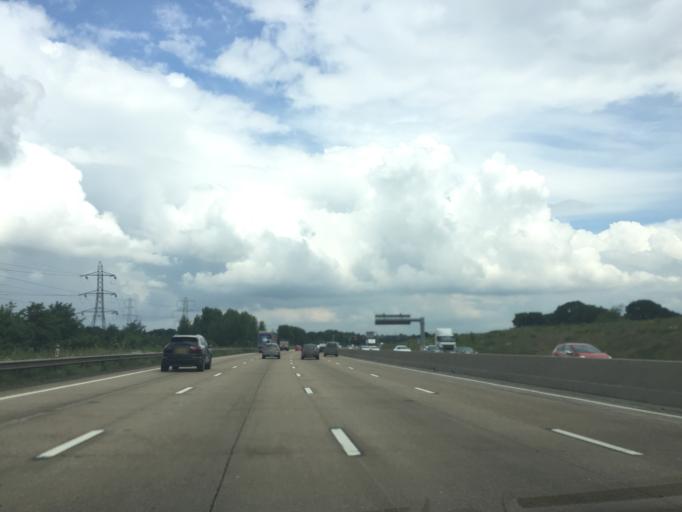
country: GB
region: England
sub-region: Greater London
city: Hadley Wood
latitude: 51.6868
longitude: -0.1423
